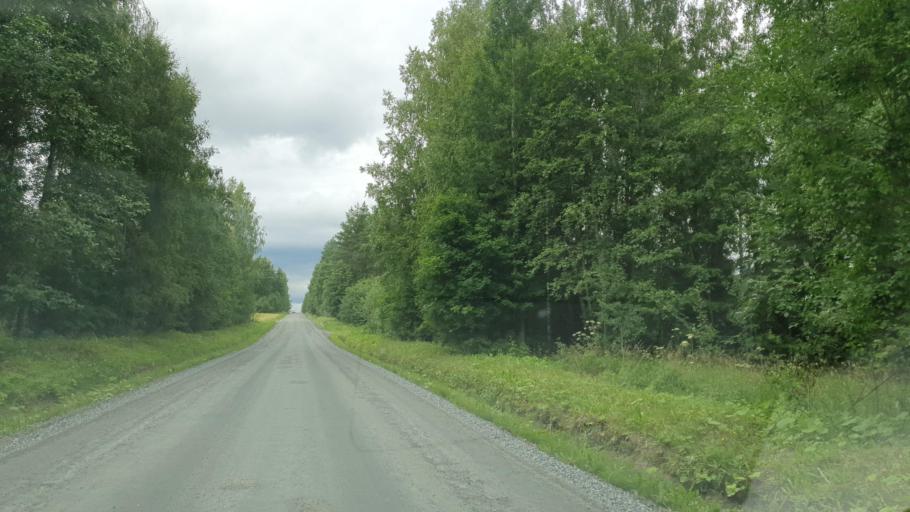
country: FI
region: Northern Savo
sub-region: Ylae-Savo
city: Iisalmi
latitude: 63.5206
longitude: 27.0981
